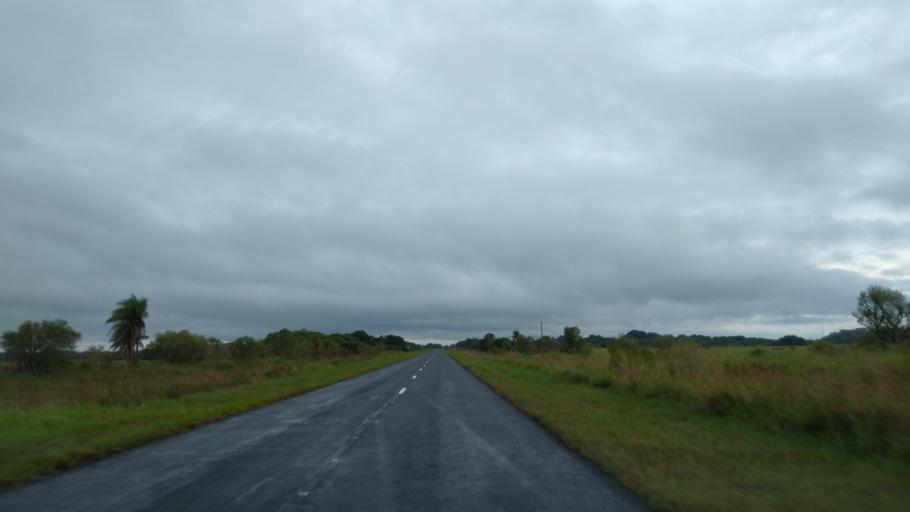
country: AR
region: Corrientes
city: Loreto
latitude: -27.6876
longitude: -57.2141
